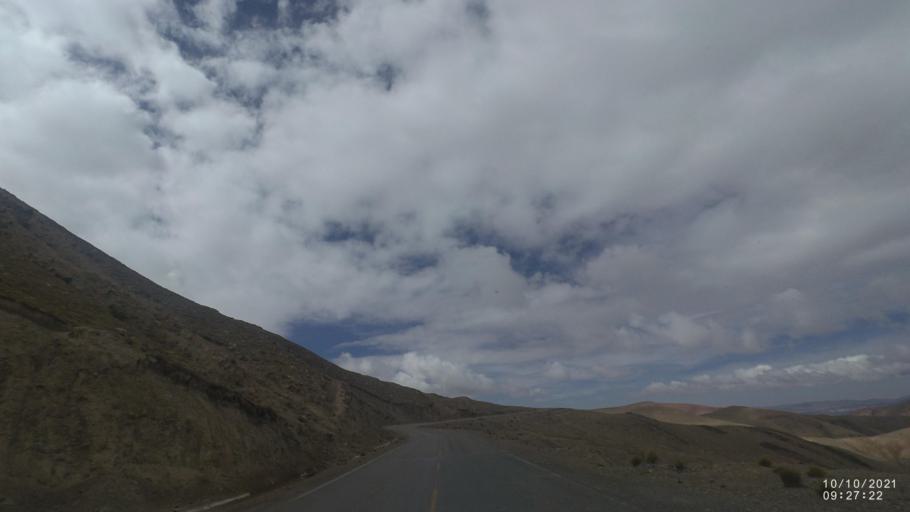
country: BO
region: La Paz
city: Quime
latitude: -17.0991
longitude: -67.3243
